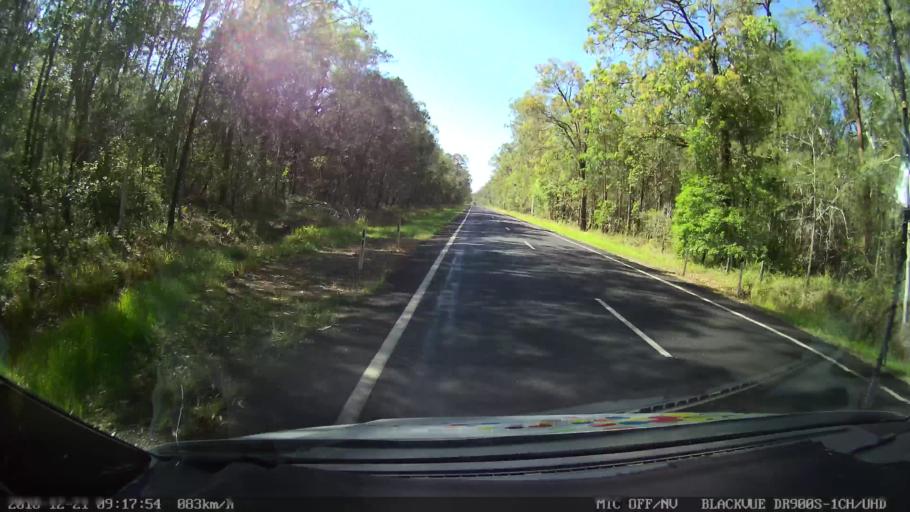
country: AU
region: New South Wales
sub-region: Clarence Valley
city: Maclean
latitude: -29.2978
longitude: 152.9922
